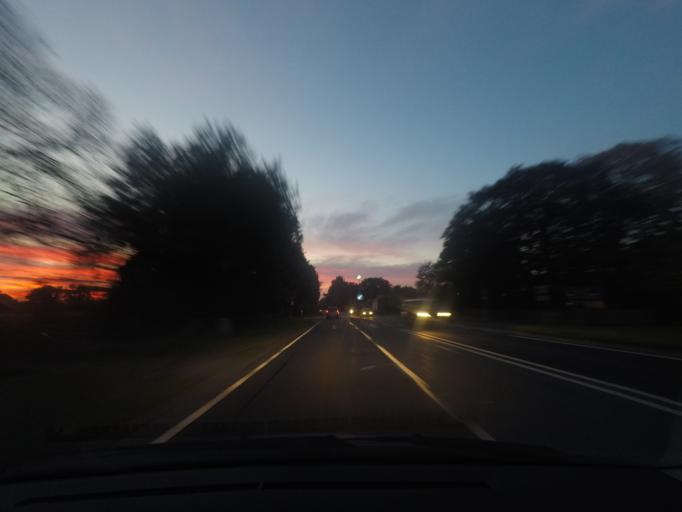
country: GB
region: England
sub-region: East Riding of Yorkshire
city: Pocklington
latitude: 53.9289
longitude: -0.8200
